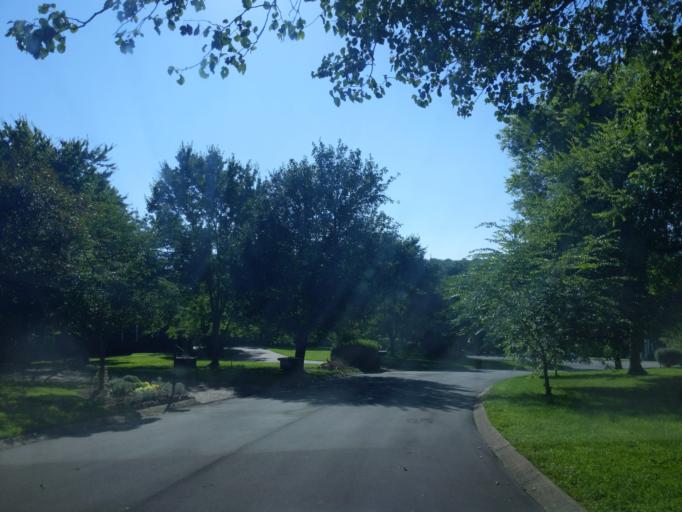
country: US
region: Tennessee
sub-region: Williamson County
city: Brentwood Estates
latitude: 36.0224
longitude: -86.7572
